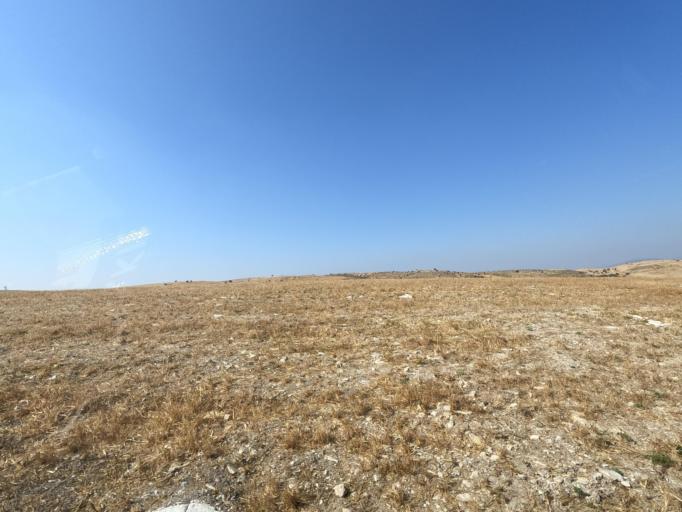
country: CY
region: Lefkosia
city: Lympia
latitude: 34.9813
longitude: 33.4826
